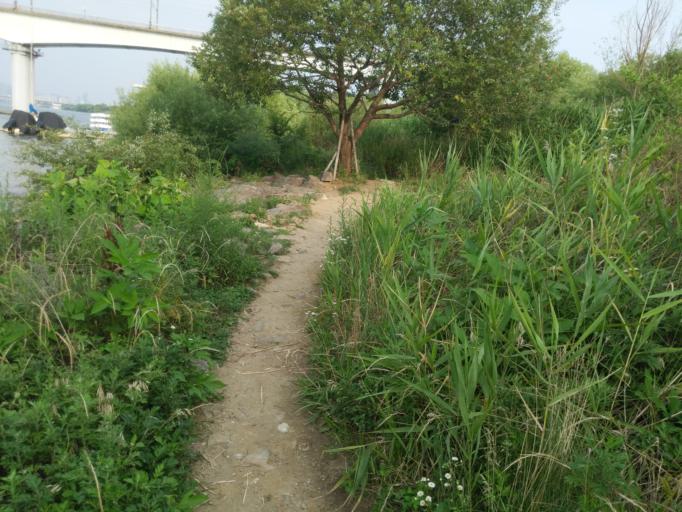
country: KR
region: Gyeonggi-do
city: Kwangmyong
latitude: 37.5386
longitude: 126.9037
